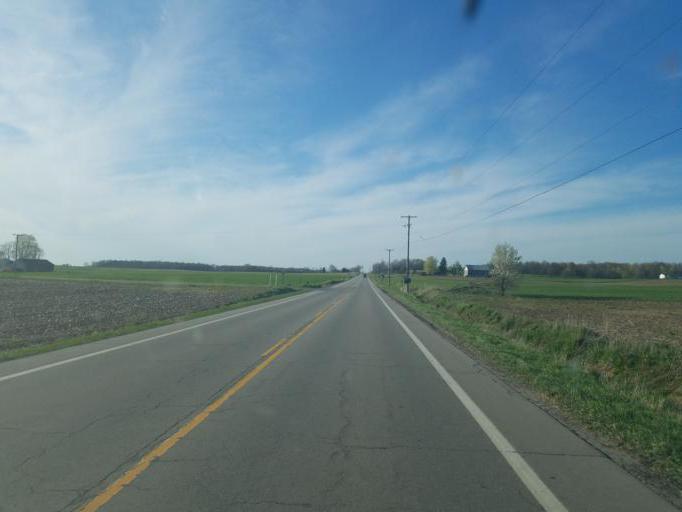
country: US
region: Ohio
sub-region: Ashland County
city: Ashland
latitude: 40.9230
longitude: -82.3463
